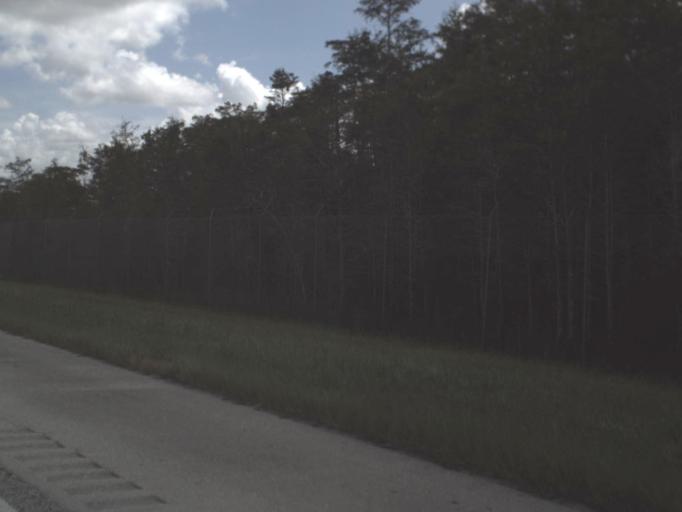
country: US
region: Florida
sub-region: Collier County
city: Immokalee
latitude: 26.1691
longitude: -81.0374
